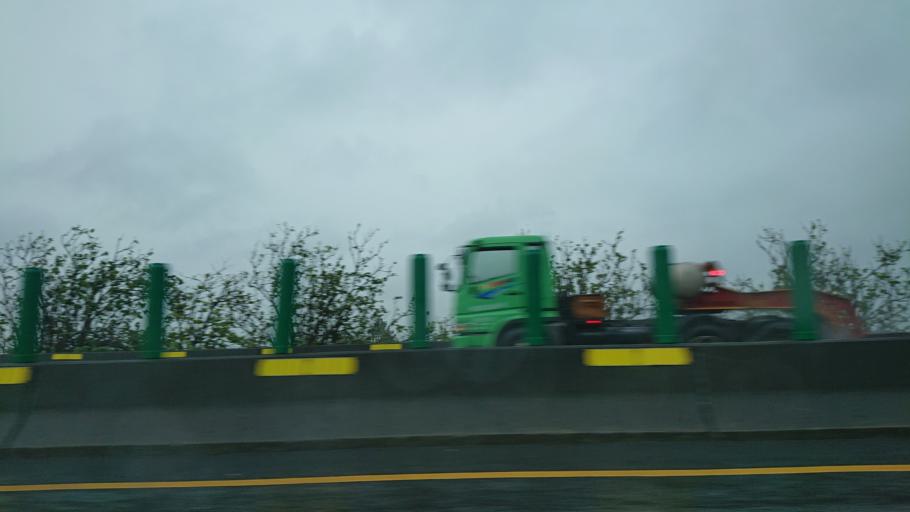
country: TW
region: Taiwan
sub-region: Chiayi
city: Taibao
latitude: 23.7179
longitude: 120.2119
